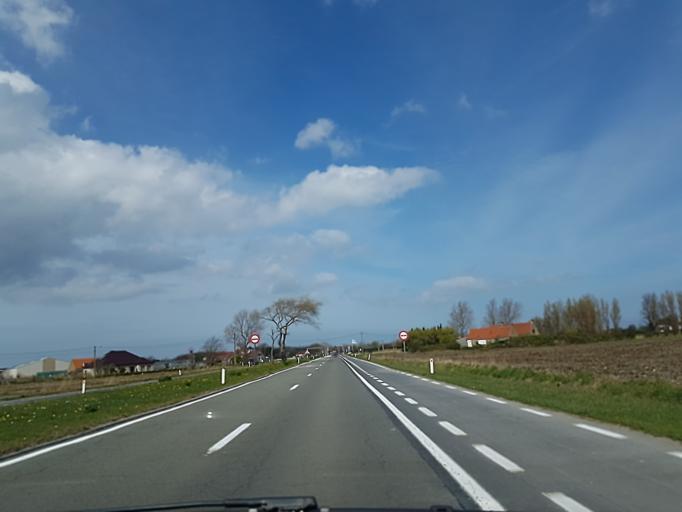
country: BE
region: Flanders
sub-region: Provincie West-Vlaanderen
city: Nieuwpoort
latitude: 51.1508
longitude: 2.7502
